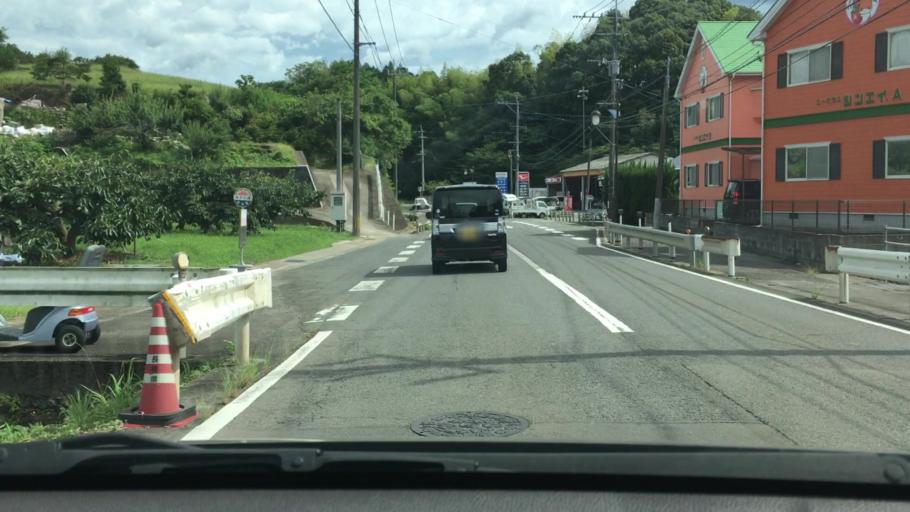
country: JP
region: Nagasaki
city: Togitsu
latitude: 32.9398
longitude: 129.7819
